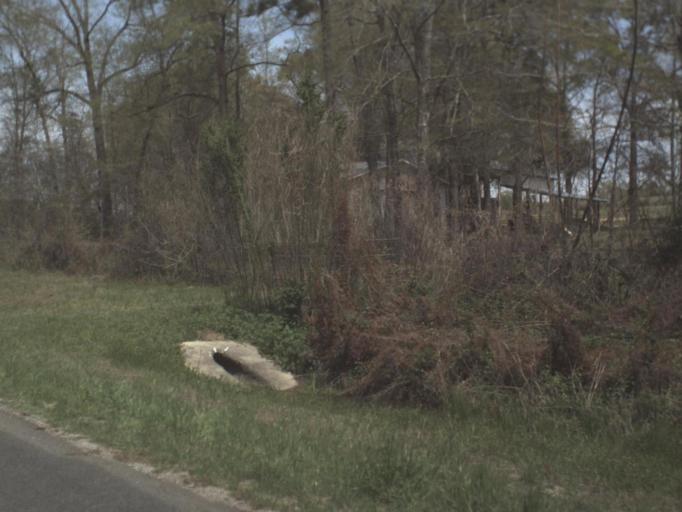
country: US
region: Alabama
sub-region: Geneva County
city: Geneva
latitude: 30.9140
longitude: -85.9593
